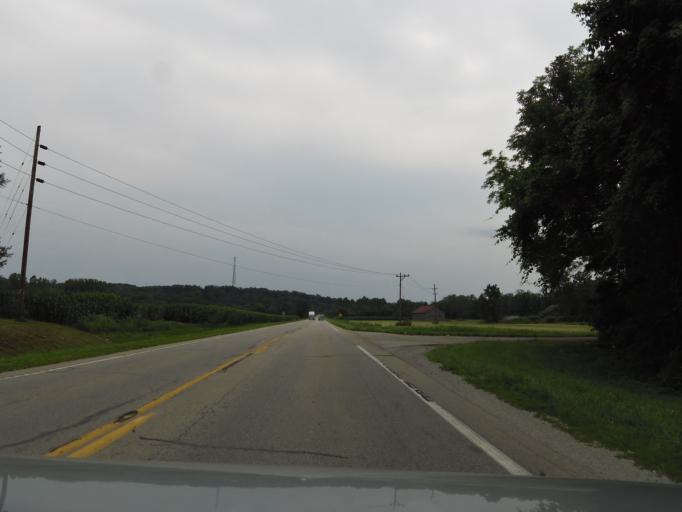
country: US
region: Ohio
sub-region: Brown County
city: Mount Orab
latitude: 38.9555
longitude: -83.9121
